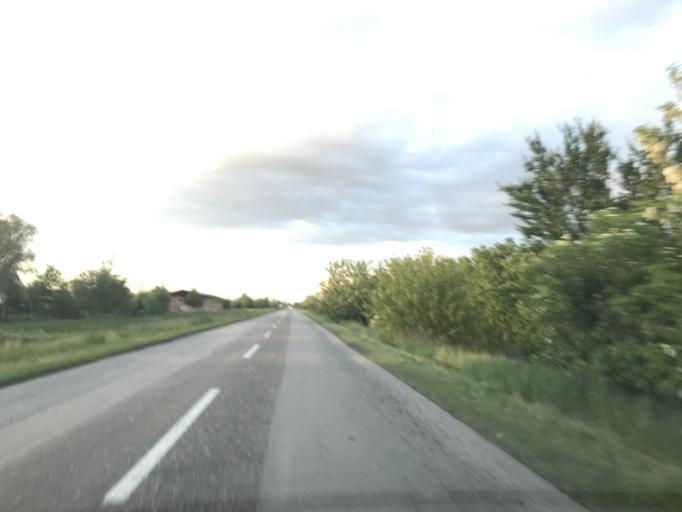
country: RS
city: Banatsko Karadordevo
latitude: 45.5861
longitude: 20.5526
